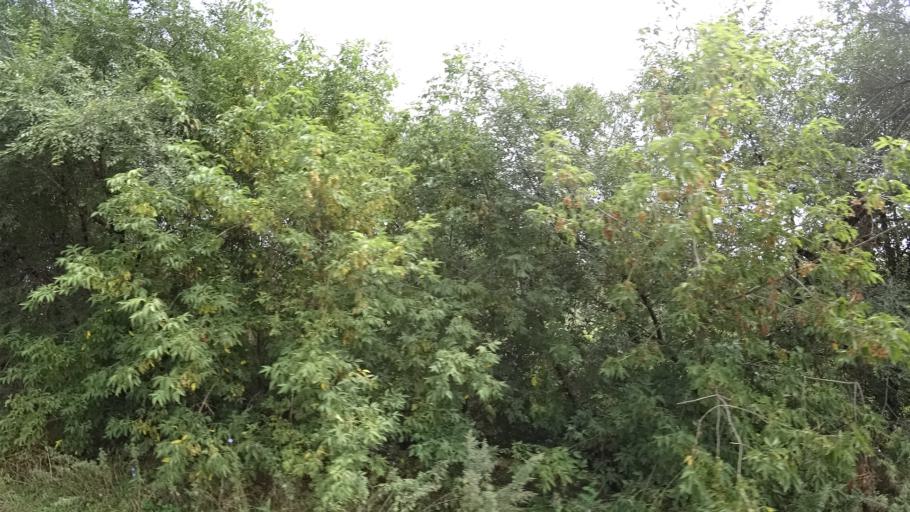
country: RU
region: Primorskiy
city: Monastyrishche
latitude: 44.1865
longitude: 132.4829
